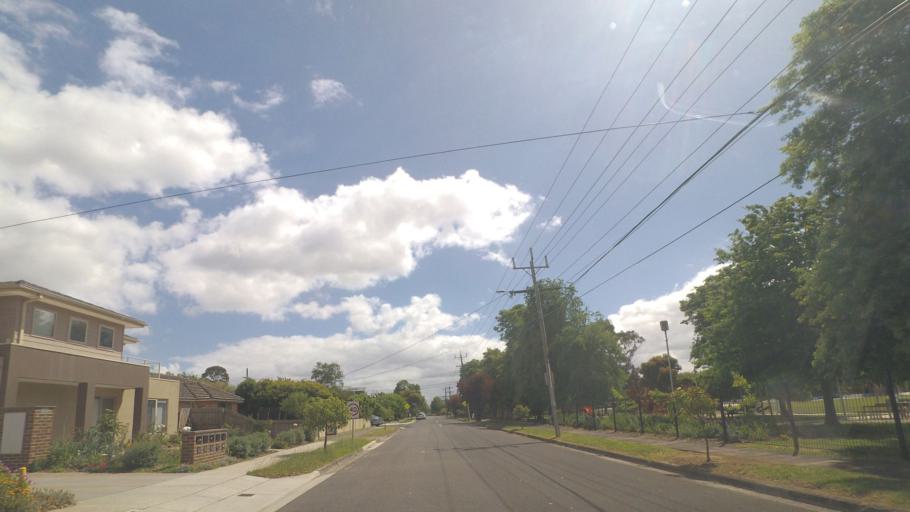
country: AU
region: Victoria
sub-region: Knox
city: Boronia
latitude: -37.8602
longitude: 145.2783
